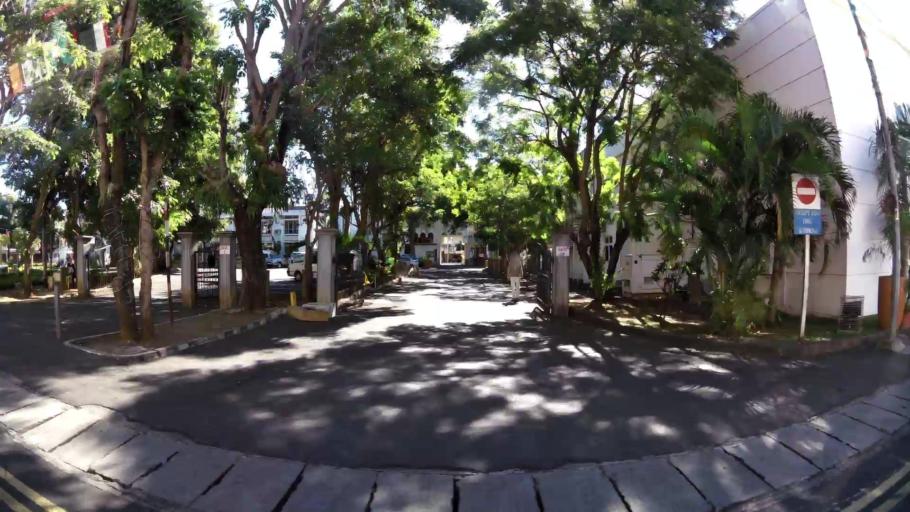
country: MU
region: Plaines Wilhems
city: Quatre Bornes
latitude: -20.2651
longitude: 57.4796
